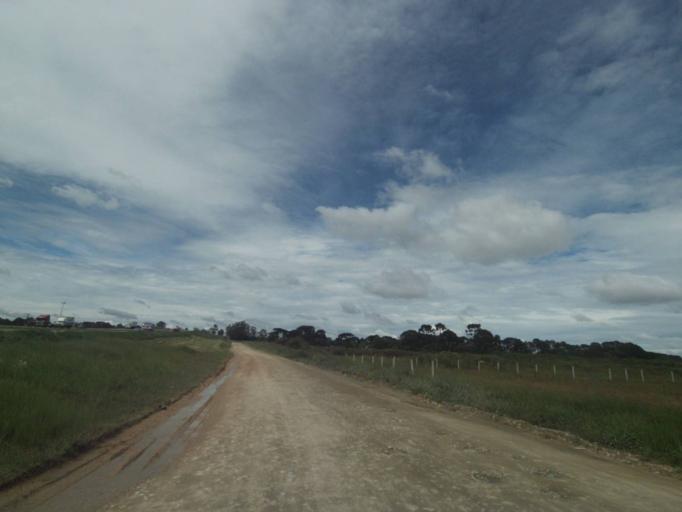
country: BR
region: Parana
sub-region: Sao Jose Dos Pinhais
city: Sao Jose dos Pinhais
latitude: -25.5294
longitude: -49.1430
